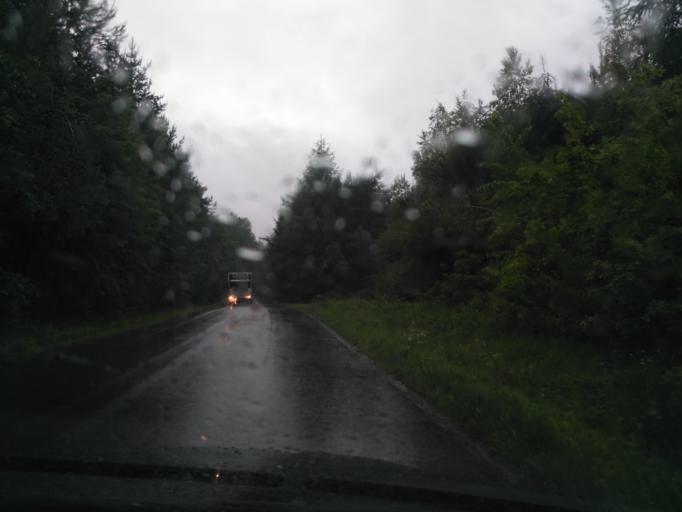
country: PL
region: Subcarpathian Voivodeship
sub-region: Powiat jasielski
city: Debowiec
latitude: 49.6634
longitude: 21.4371
